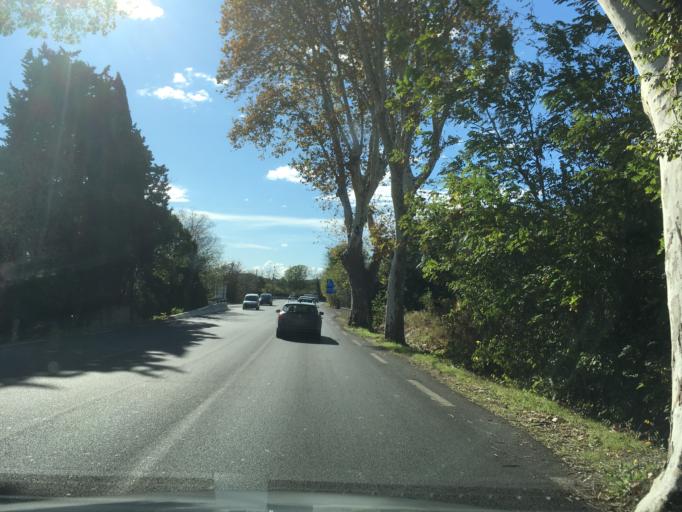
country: FR
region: Languedoc-Roussillon
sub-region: Departement de l'Herault
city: Saint-Jean-de-Vedas
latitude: 43.5867
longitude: 3.8528
